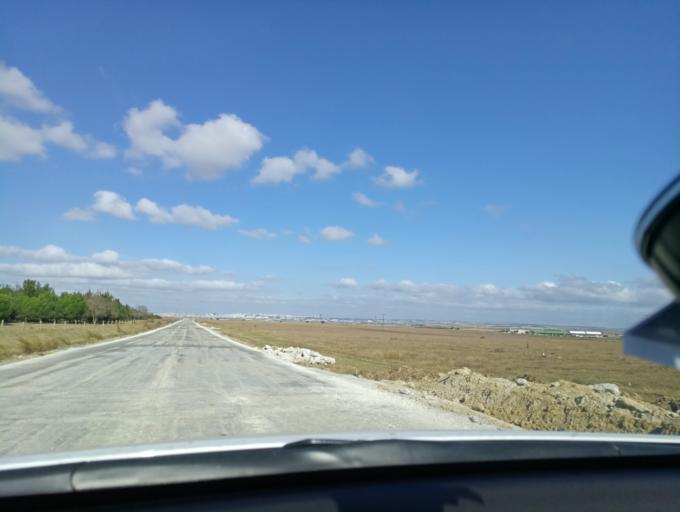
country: TR
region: Tekirdag
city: Corlu
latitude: 41.0619
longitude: 27.8343
